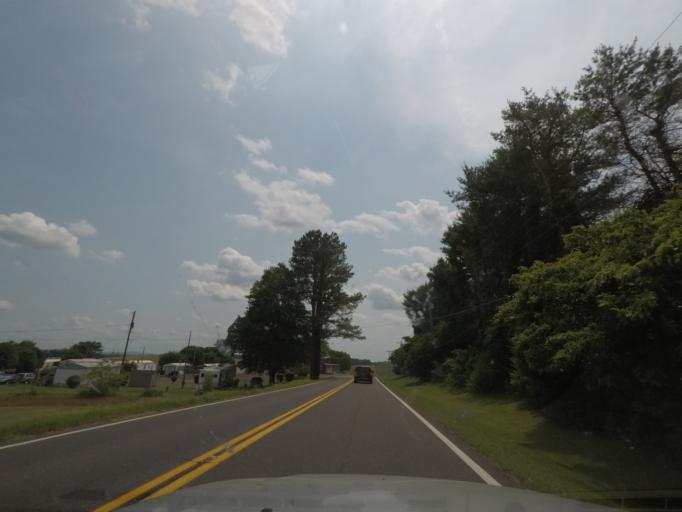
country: US
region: Virginia
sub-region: Culpeper County
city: Merrimac
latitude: 38.4271
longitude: -78.0369
